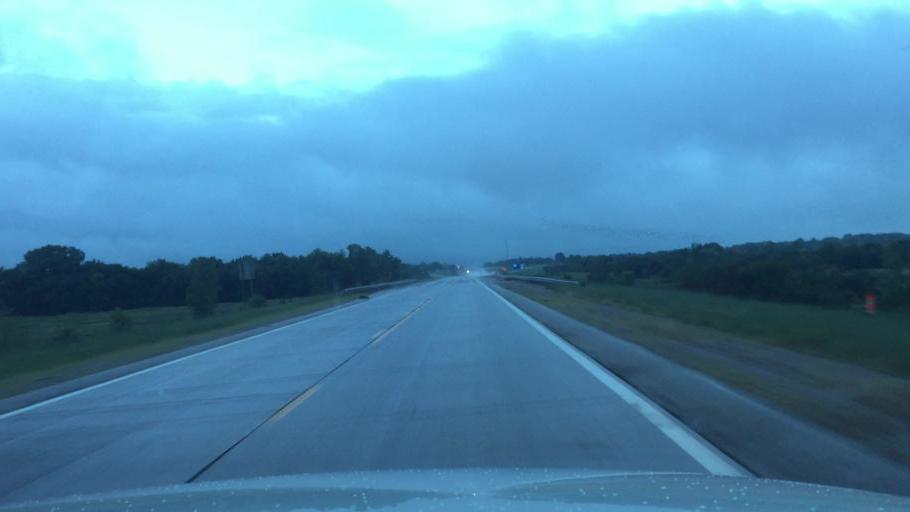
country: US
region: Kansas
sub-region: Neosho County
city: Chanute
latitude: 37.6990
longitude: -95.4794
